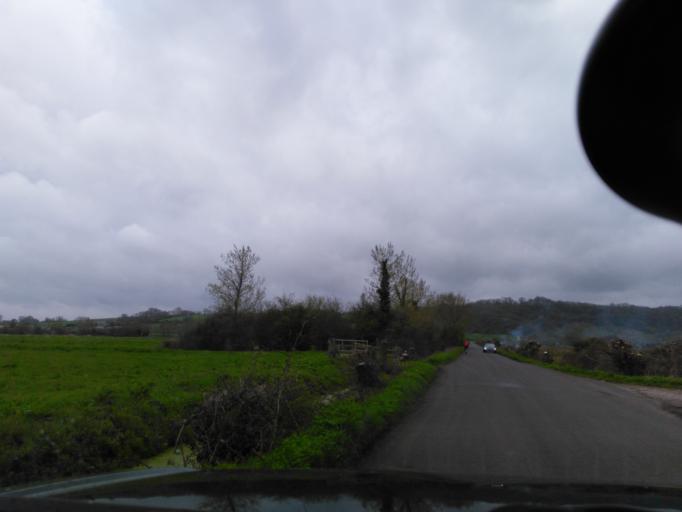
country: GB
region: England
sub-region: Somerset
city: Langport
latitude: 51.0941
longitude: -2.8204
